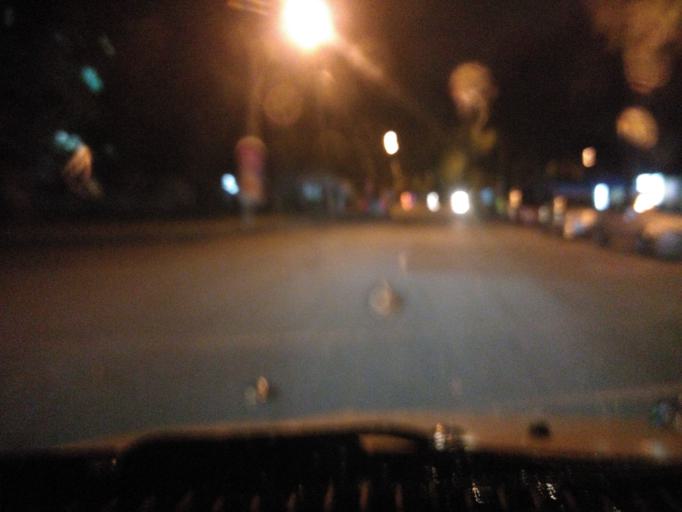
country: MY
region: Penang
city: Perai
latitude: 5.3976
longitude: 100.4021
